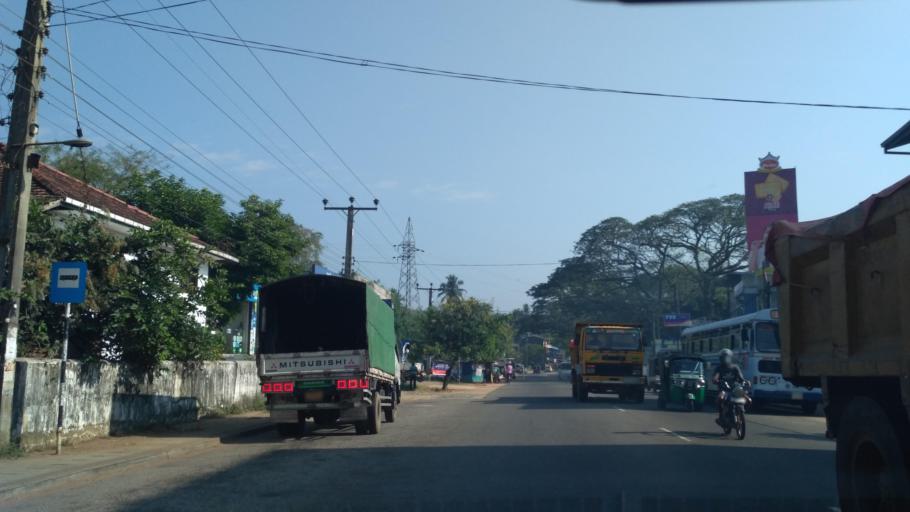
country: LK
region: North Western
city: Kuliyapitiya
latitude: 7.3326
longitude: 80.1249
